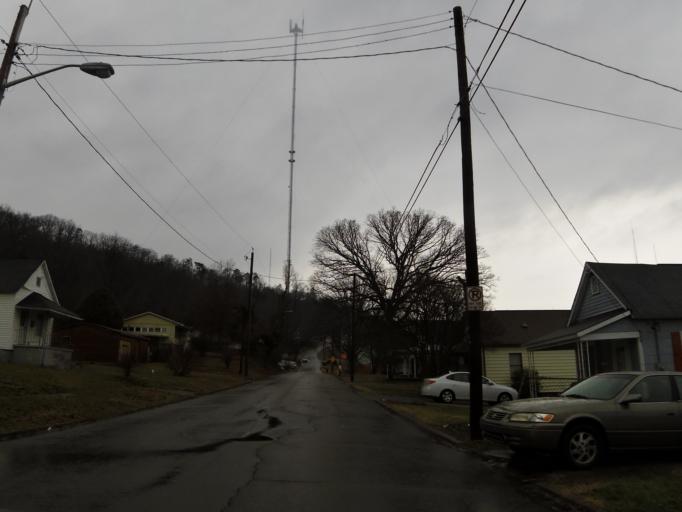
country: US
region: Tennessee
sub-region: Knox County
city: Knoxville
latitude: 35.9902
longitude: -83.9565
